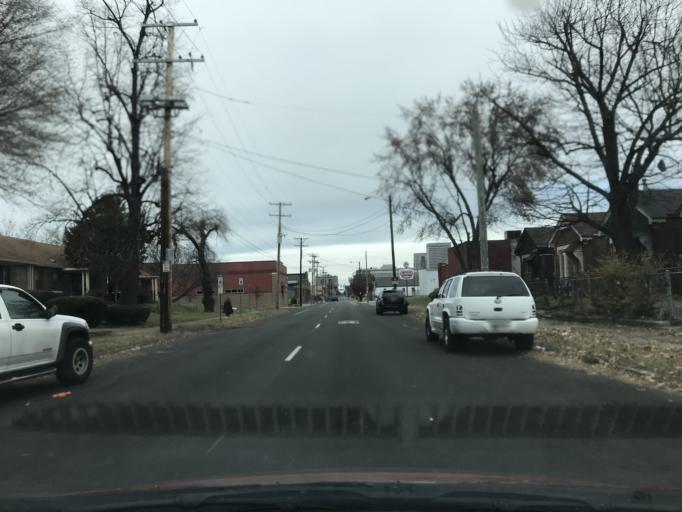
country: US
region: Kentucky
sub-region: Jefferson County
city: Louisville
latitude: 38.2410
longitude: -85.7643
